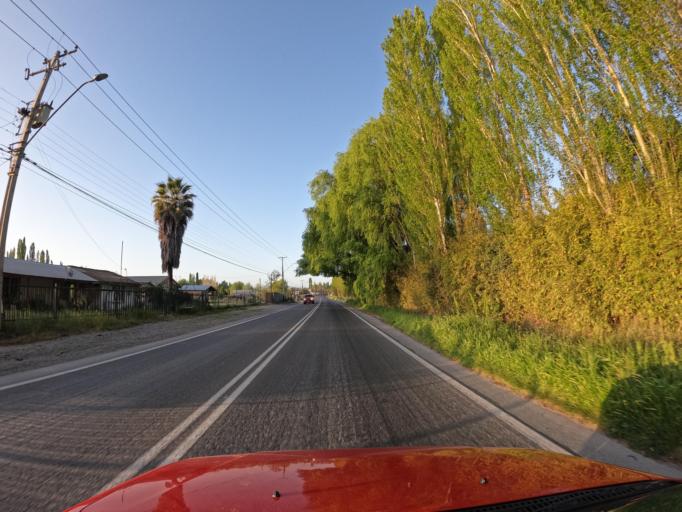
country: CL
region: O'Higgins
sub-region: Provincia de Cachapoal
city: San Vicente
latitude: -34.1867
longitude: -71.4024
